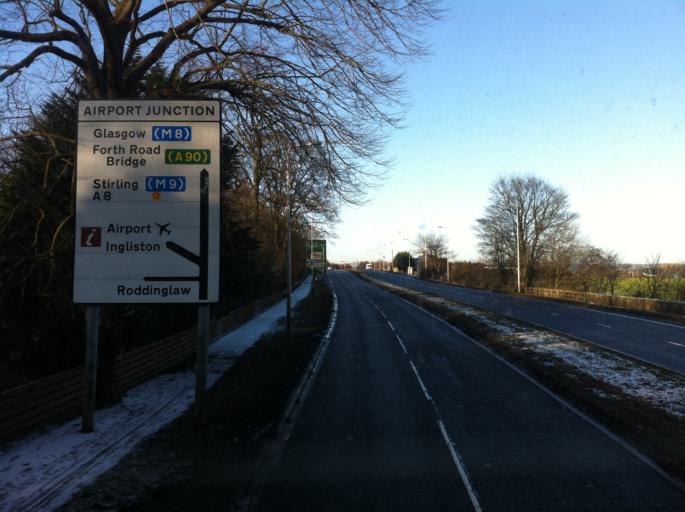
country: GB
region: Scotland
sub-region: Edinburgh
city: Ratho
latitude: 55.9366
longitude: -3.3480
